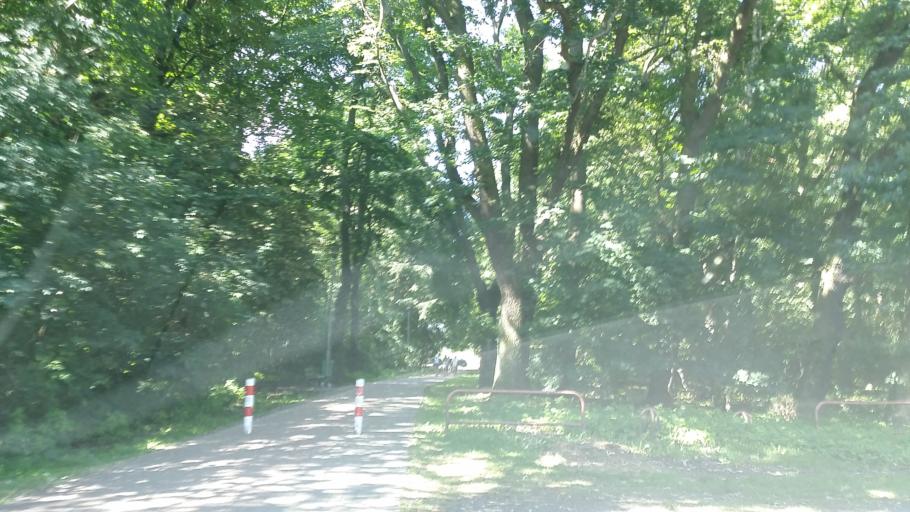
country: PL
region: West Pomeranian Voivodeship
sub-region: Powiat kolobrzeski
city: Kolobrzeg
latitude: 54.1740
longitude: 15.5369
